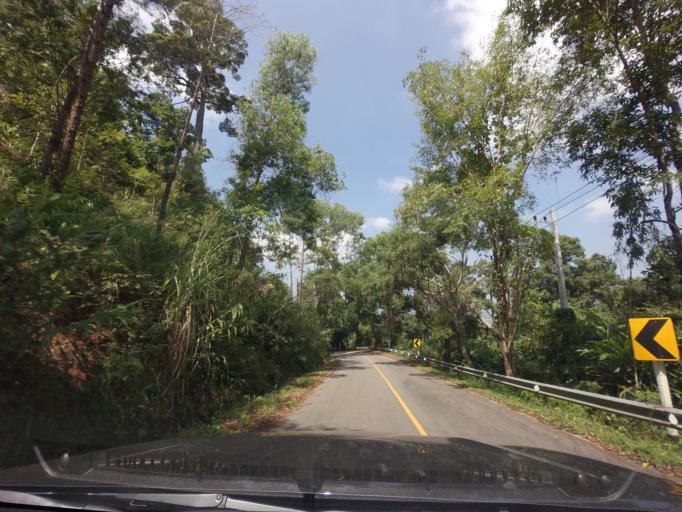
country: TH
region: Loei
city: Na Haeo
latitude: 17.4935
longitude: 100.8999
